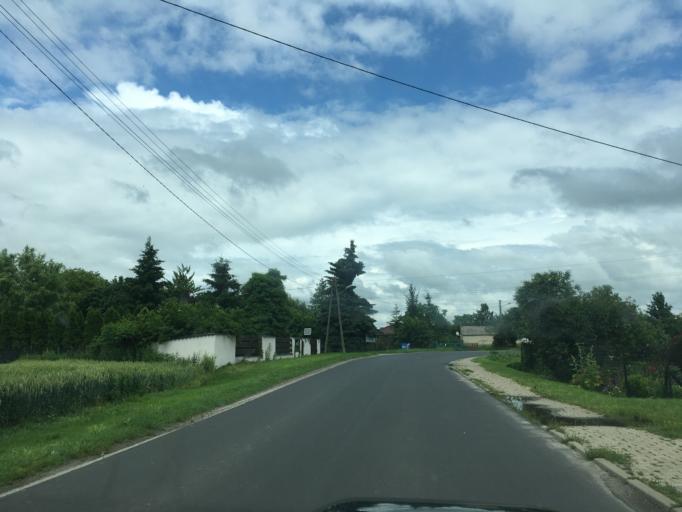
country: PL
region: Lublin Voivodeship
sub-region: Powiat swidnicki
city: Swidnik
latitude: 51.2043
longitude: 22.7349
